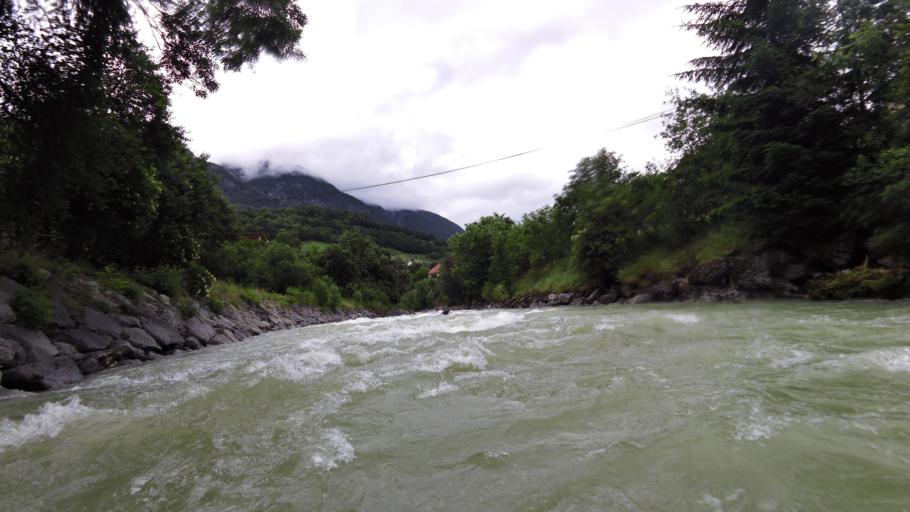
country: AT
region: Tyrol
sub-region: Politischer Bezirk Landeck
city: Pians
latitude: 47.1321
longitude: 10.5091
